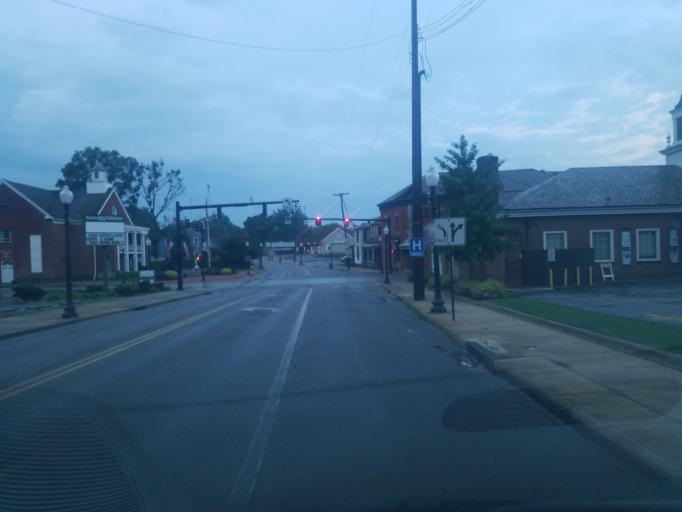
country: US
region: Ohio
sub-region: Columbiana County
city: Salem
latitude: 40.9015
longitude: -80.8516
